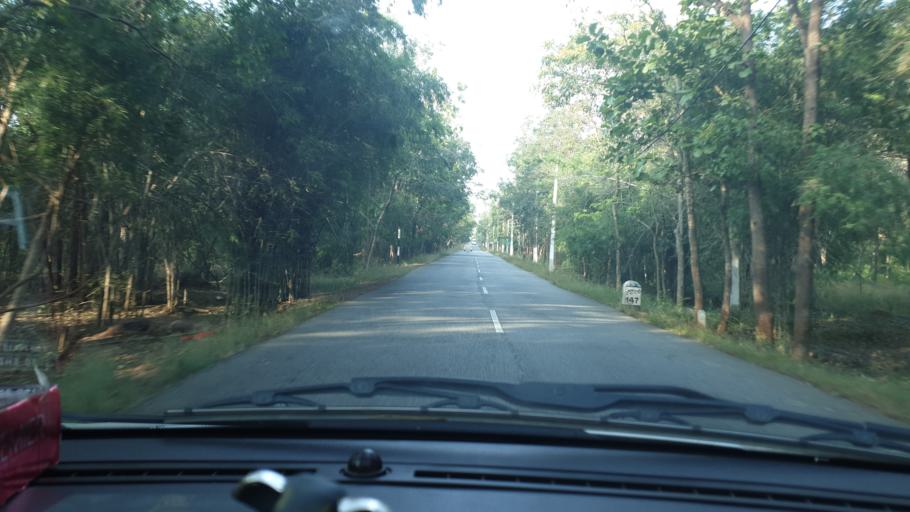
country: IN
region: Andhra Pradesh
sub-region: Kurnool
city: Srisailam
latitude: 16.2973
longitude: 78.7311
